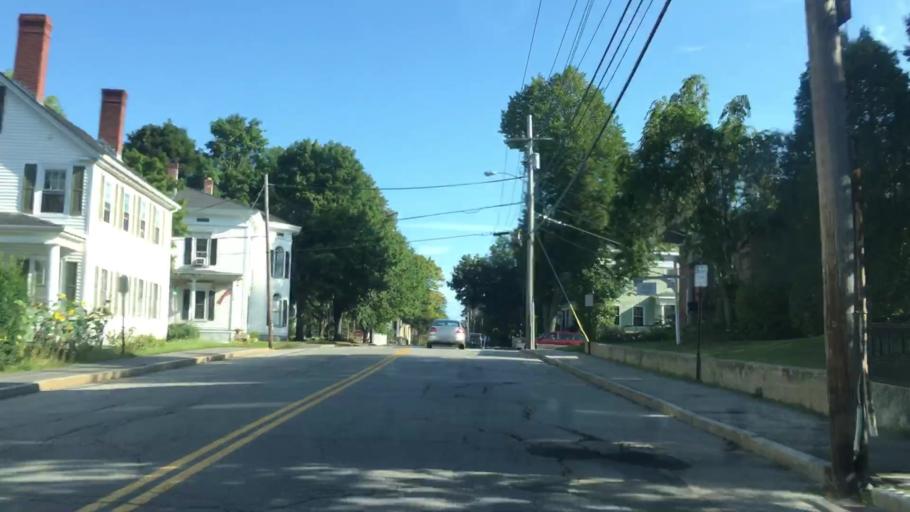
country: US
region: Maine
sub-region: Sagadahoc County
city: Bath
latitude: 43.9167
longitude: -69.8159
